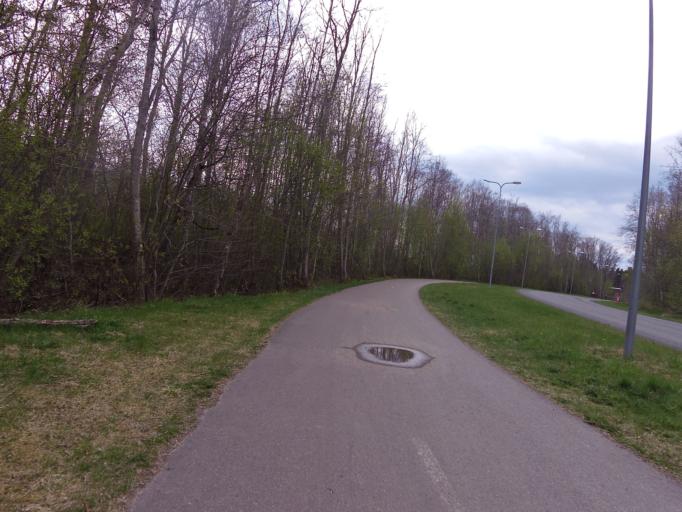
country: EE
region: Harju
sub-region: Kiili vald
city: Kiili
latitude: 59.3639
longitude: 24.8163
